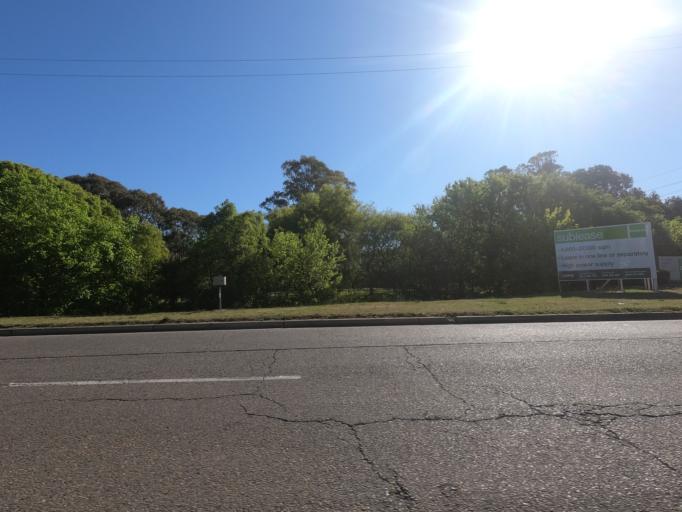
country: AU
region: New South Wales
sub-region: Fairfield
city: Liverpool
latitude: -33.9354
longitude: 150.9350
